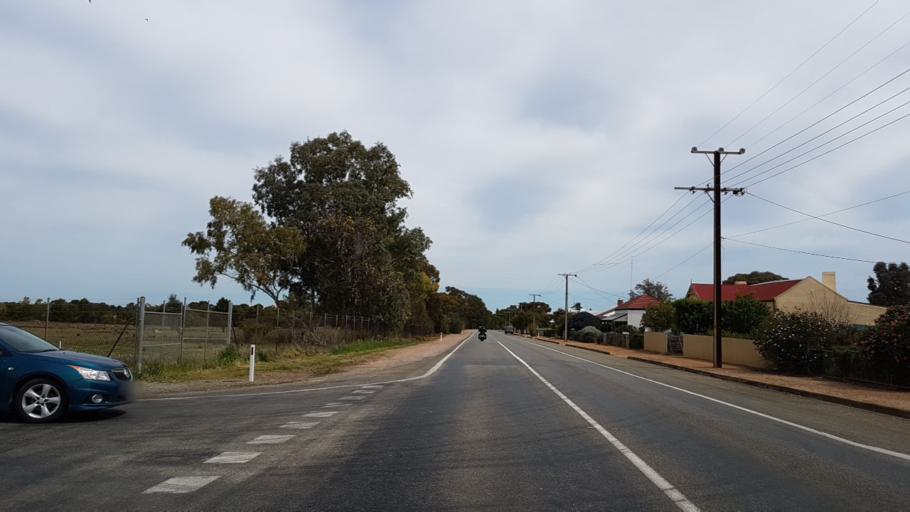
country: AU
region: South Australia
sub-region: Port Pirie City and Dists
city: Crystal Brook
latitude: -33.2616
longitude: 138.3544
